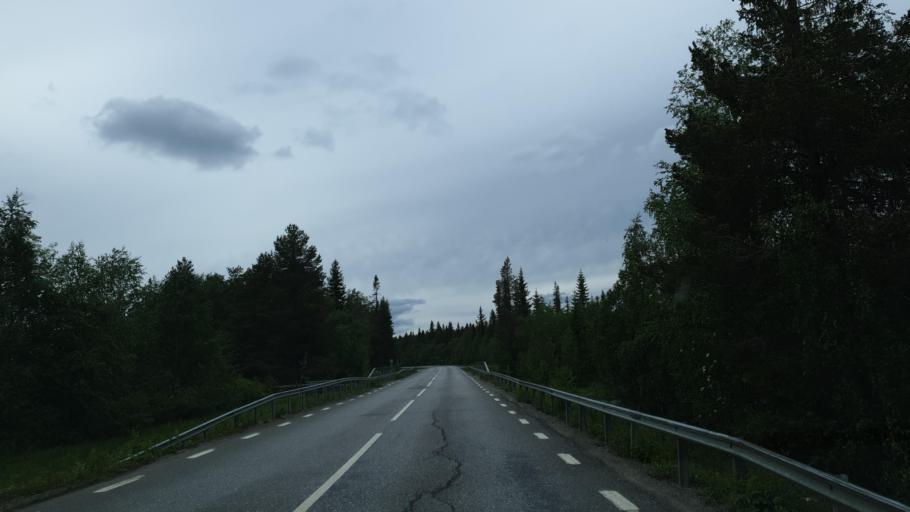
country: SE
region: Vaesterbotten
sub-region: Sorsele Kommun
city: Sorsele
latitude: 65.5051
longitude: 17.2590
